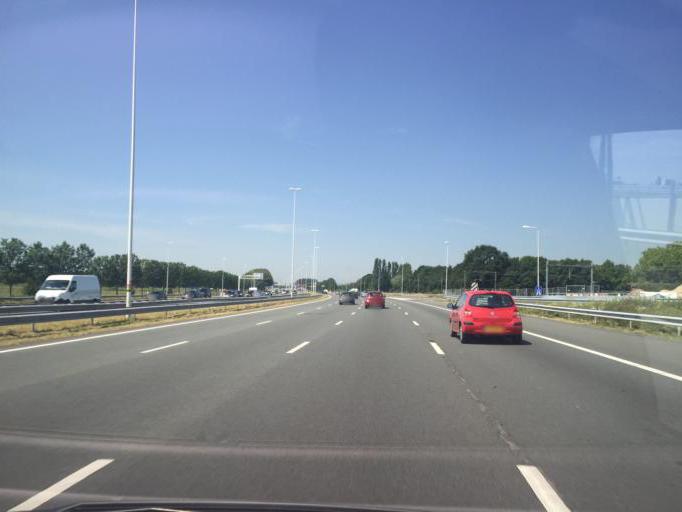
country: NL
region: Utrecht
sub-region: Gemeente Bunnik
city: Bunnik
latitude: 52.0623
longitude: 5.1890
